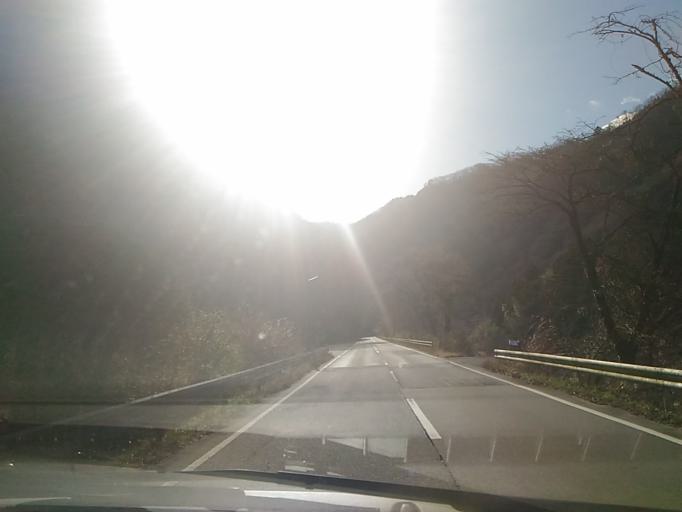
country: JP
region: Fukushima
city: Ishikawa
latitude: 37.0329
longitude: 140.6489
